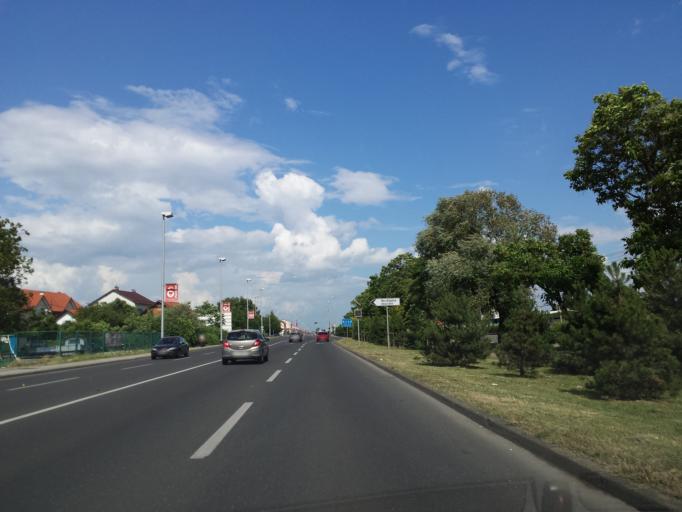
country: HR
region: Grad Zagreb
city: Dubrava
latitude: 45.8190
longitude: 16.0518
